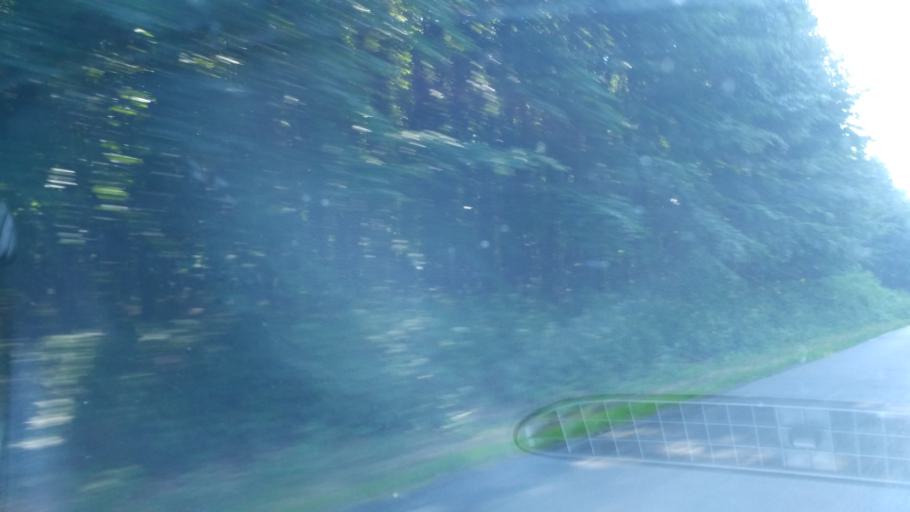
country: PL
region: Subcarpathian Voivodeship
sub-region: Powiat jaroslawski
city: Rokietnica
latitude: 49.9289
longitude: 22.6777
